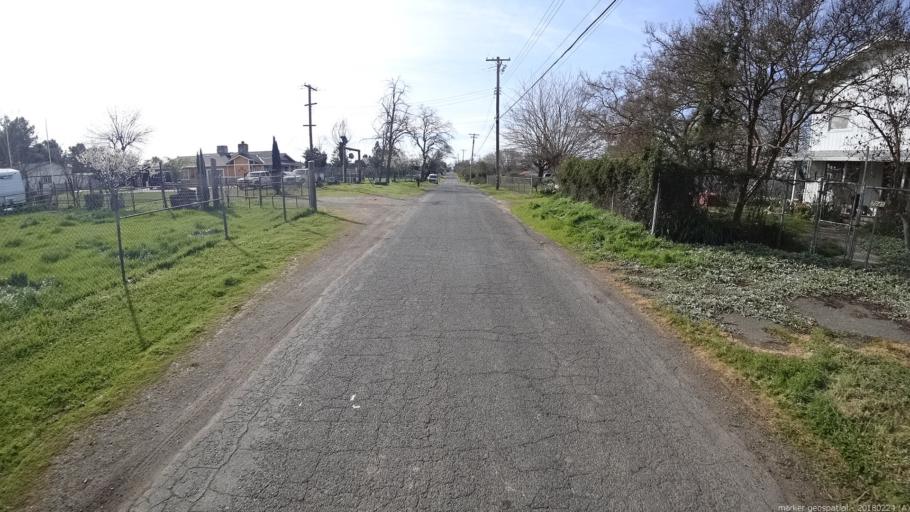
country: US
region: California
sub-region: Sacramento County
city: Rio Linda
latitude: 38.6963
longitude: -121.4615
